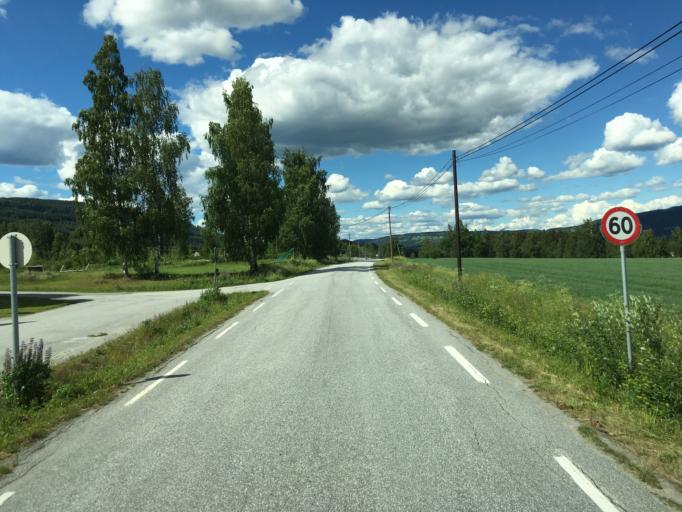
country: NO
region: Oppland
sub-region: Sondre Land
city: Hov
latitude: 60.6422
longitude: 10.3352
